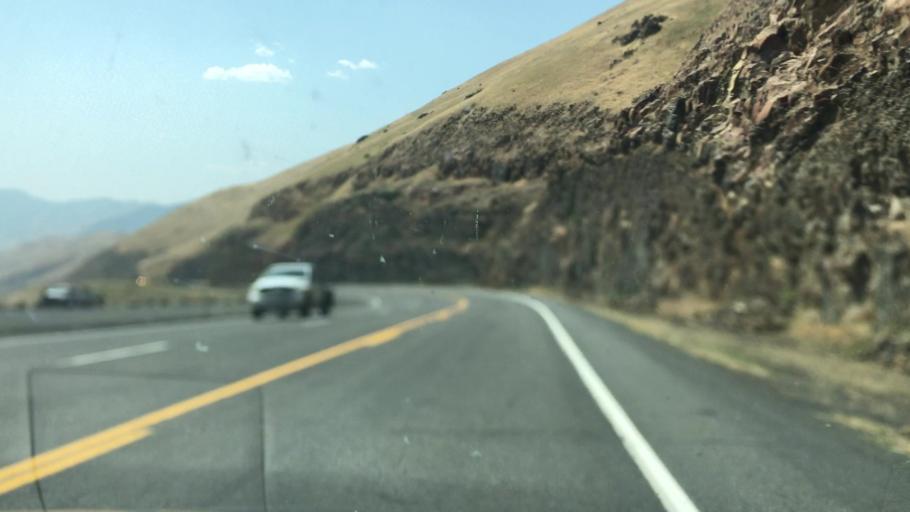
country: US
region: Idaho
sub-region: Idaho County
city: Grangeville
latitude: 45.8192
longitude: -116.2727
